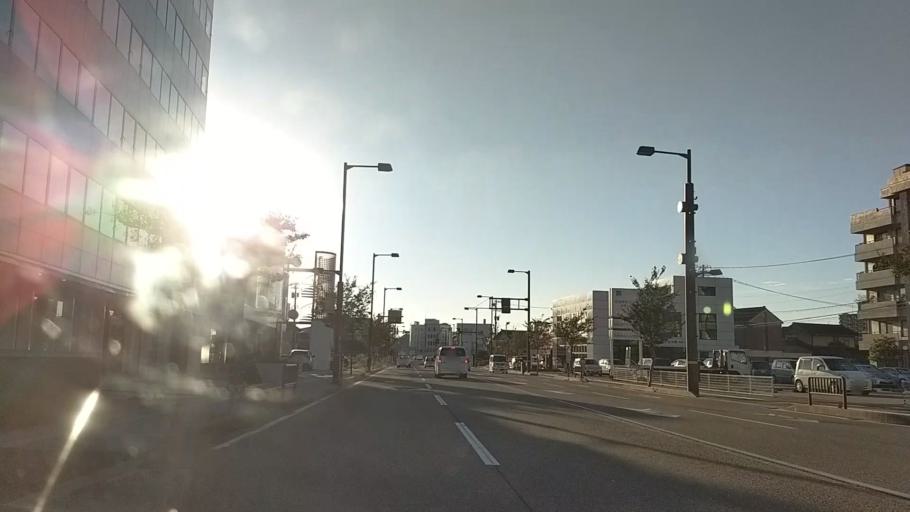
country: JP
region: Ishikawa
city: Nonoichi
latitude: 36.5586
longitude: 136.6413
